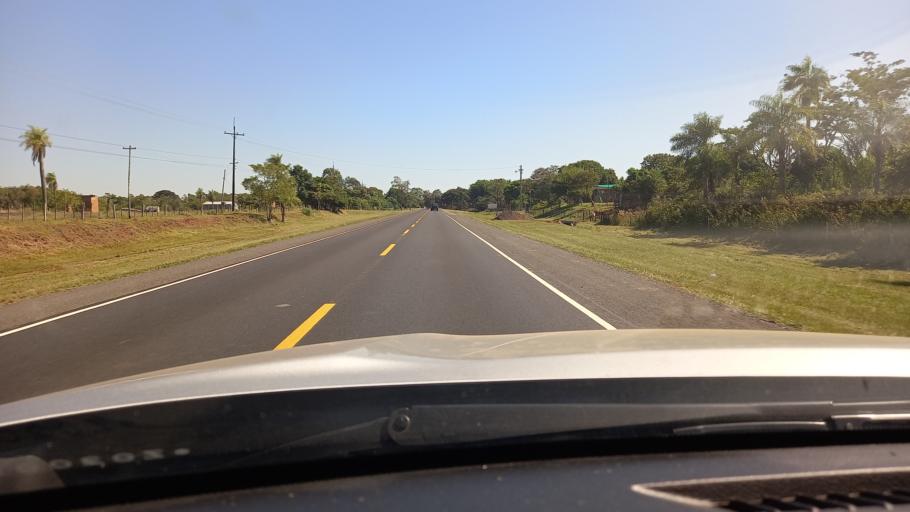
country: PY
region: Itapua
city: General Delgado
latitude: -27.0772
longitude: -56.5735
